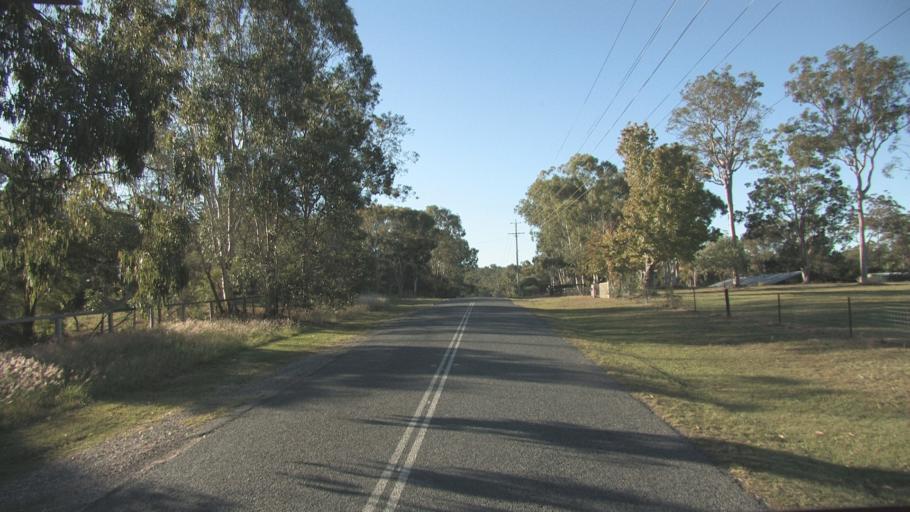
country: AU
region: Queensland
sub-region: Logan
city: Chambers Flat
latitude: -27.7740
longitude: 153.1291
